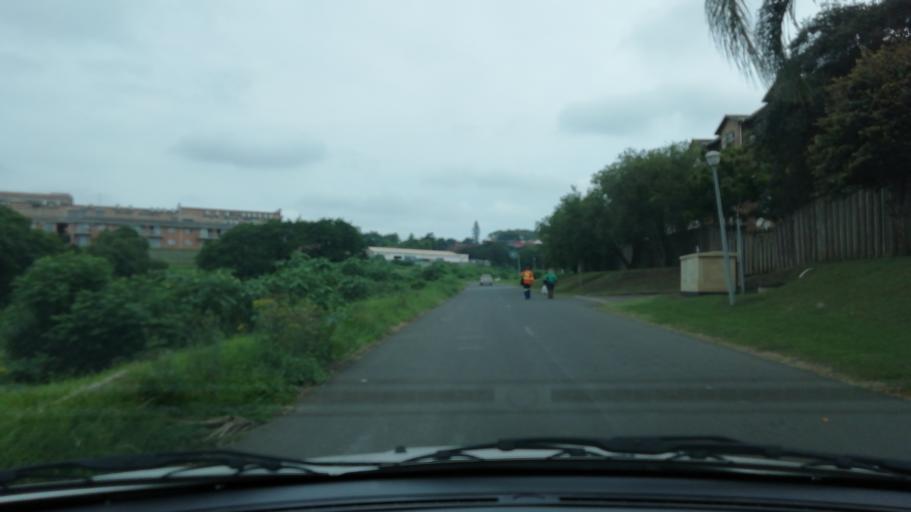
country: ZA
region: KwaZulu-Natal
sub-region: uThungulu District Municipality
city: Empangeni
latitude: -28.7405
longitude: 31.8853
